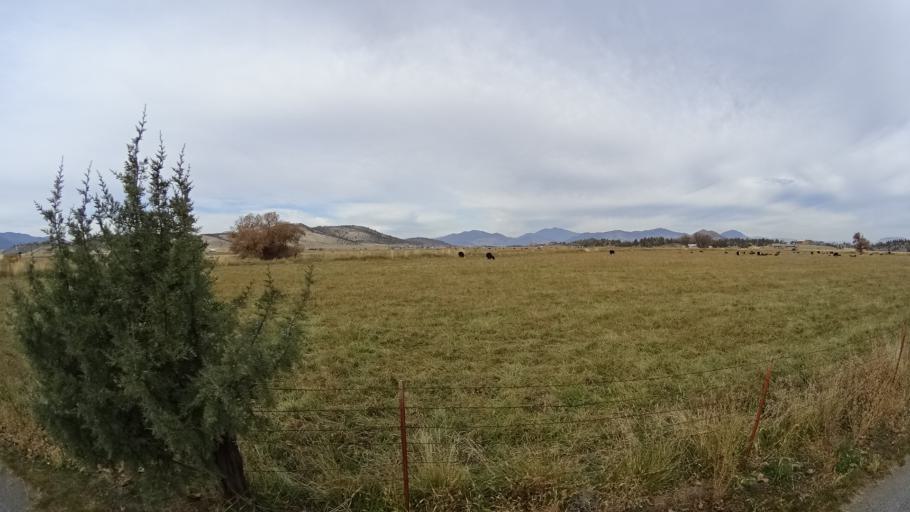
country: US
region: California
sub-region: Siskiyou County
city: Montague
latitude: 41.6592
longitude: -122.5096
